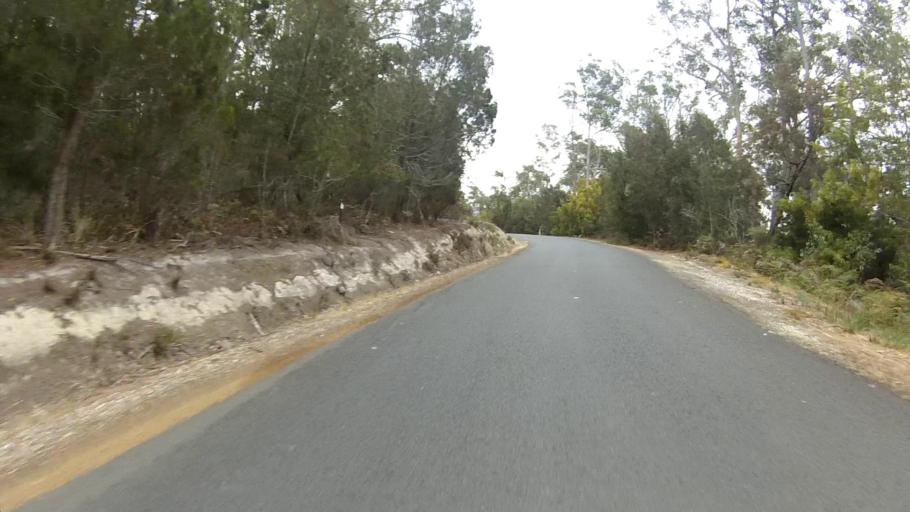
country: AU
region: Tasmania
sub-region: Huon Valley
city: Cygnet
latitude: -43.2163
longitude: 147.1036
